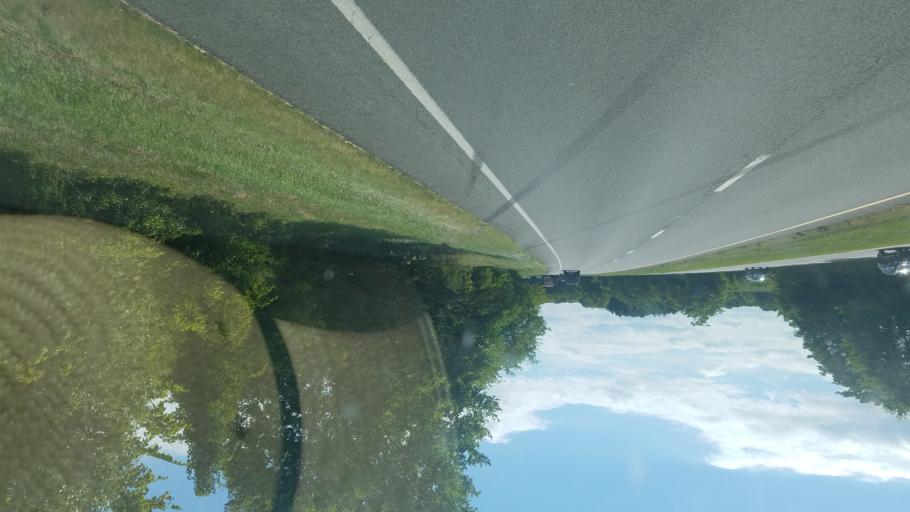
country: US
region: Virginia
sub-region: Fauquier County
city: Bealeton
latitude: 38.6017
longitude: -77.7780
